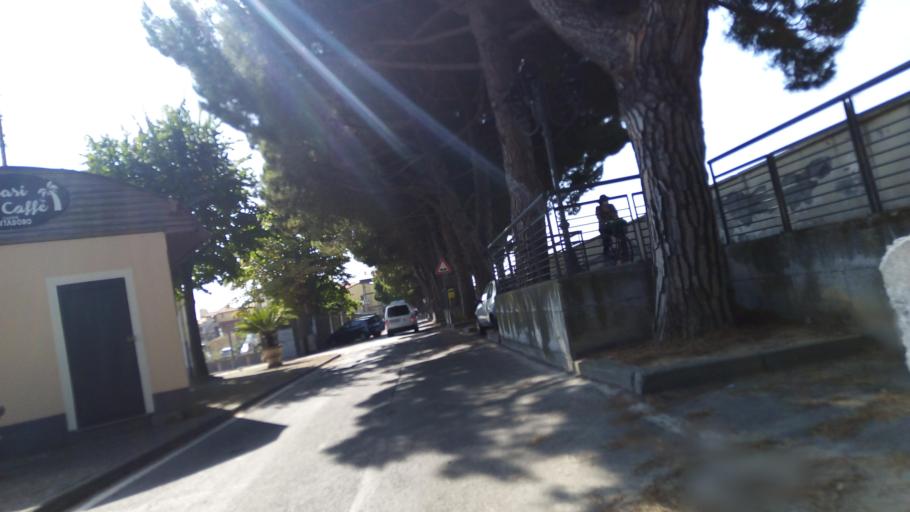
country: IT
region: Liguria
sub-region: Provincia di Savona
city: Albenga
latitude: 44.0514
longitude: 8.2076
